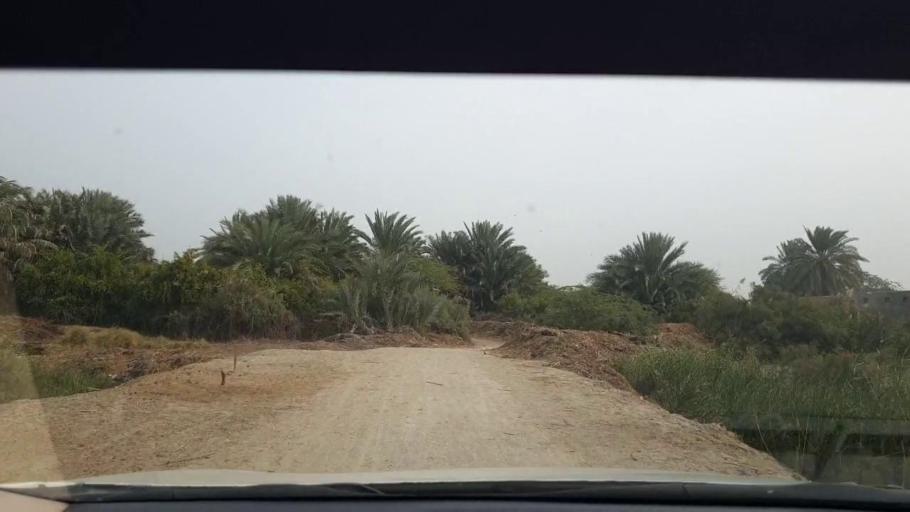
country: PK
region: Sindh
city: Berani
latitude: 25.8381
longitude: 68.8511
